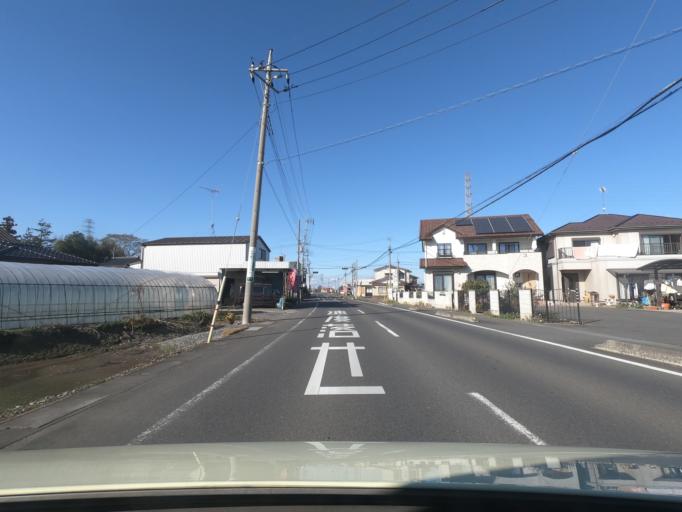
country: JP
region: Ibaraki
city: Ishige
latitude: 36.1720
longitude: 139.9879
